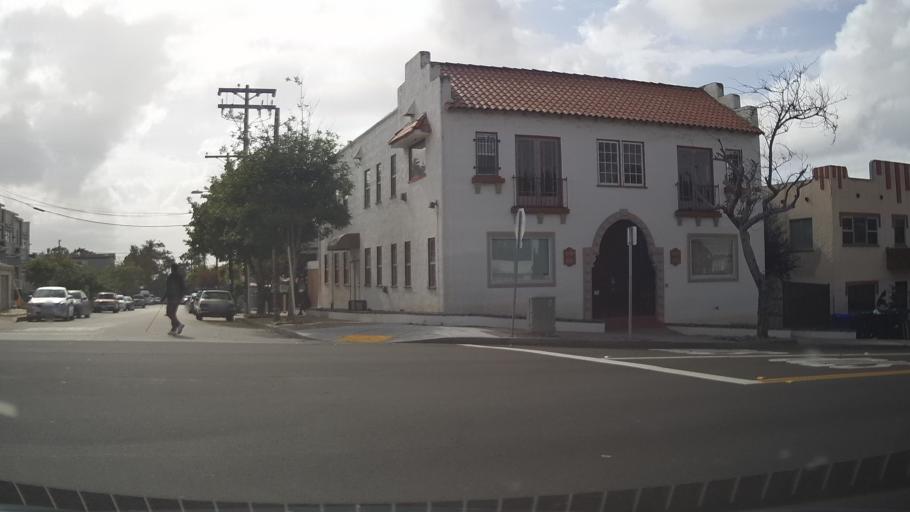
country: US
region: California
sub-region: San Diego County
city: San Diego
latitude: 32.7159
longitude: -117.1361
